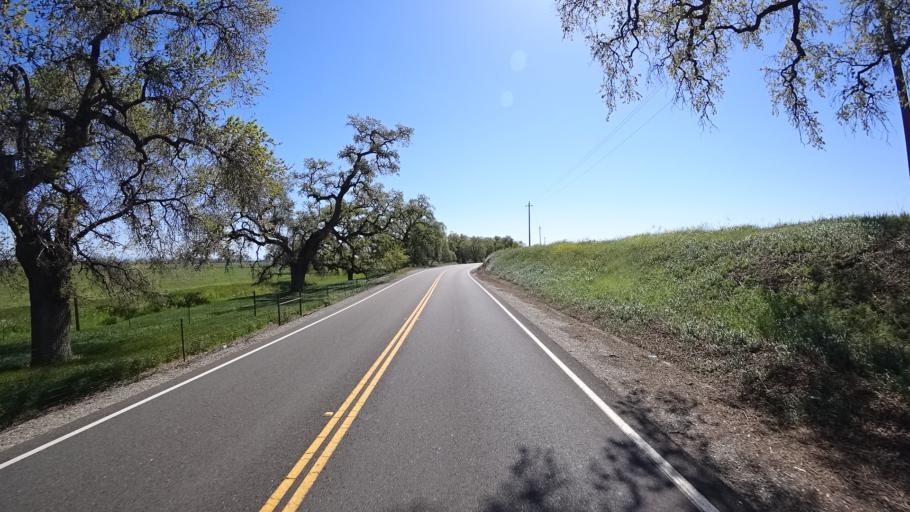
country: US
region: California
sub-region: Glenn County
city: Orland
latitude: 39.7961
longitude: -122.3158
